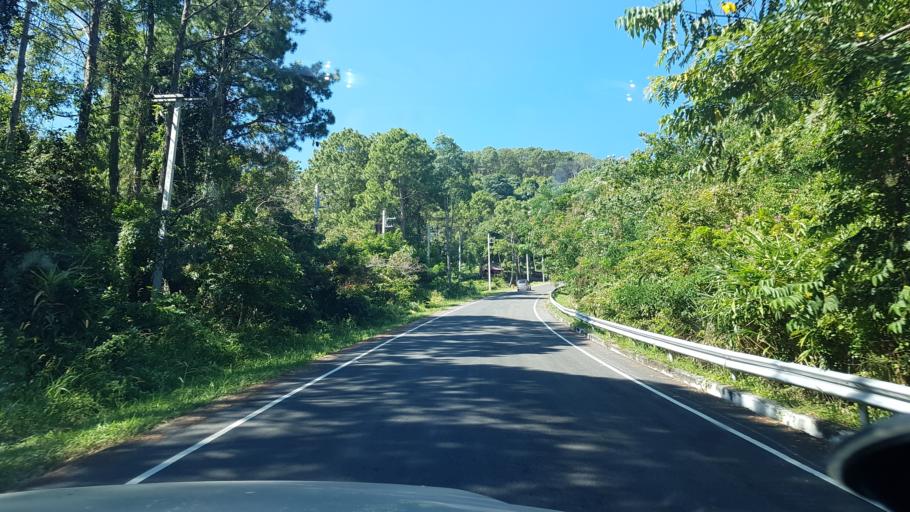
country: TH
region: Phetchabun
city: Khao Kho
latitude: 16.5525
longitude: 100.9795
